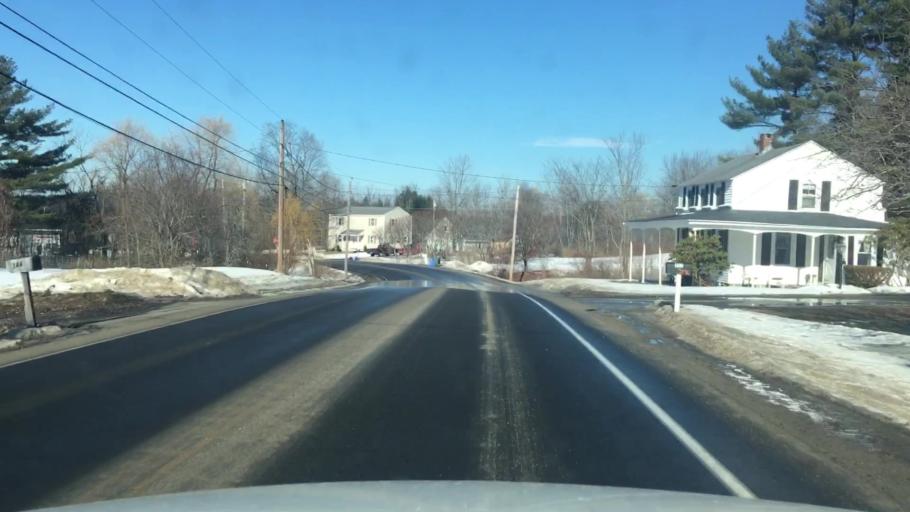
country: US
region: Maine
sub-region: Cumberland County
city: North Windham
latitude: 43.8238
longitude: -70.3879
